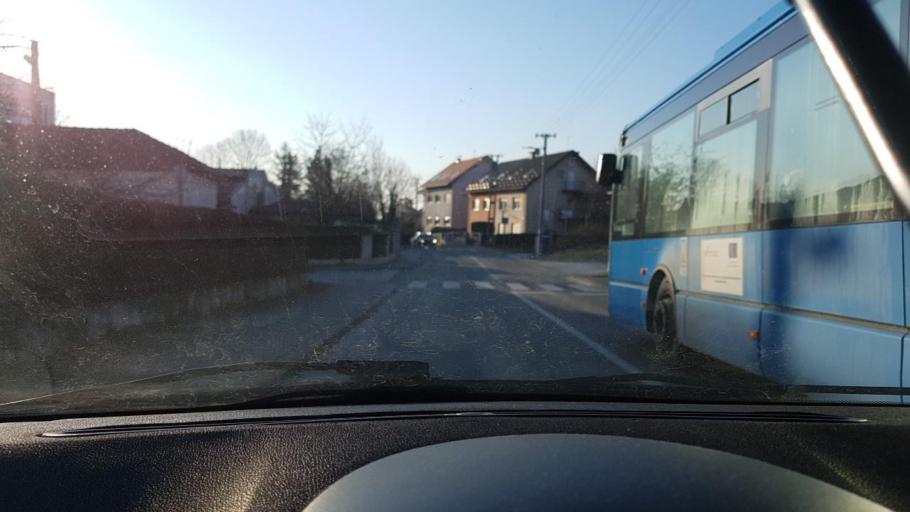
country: HR
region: Grad Zagreb
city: Zagreb
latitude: 45.8400
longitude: 16.0018
